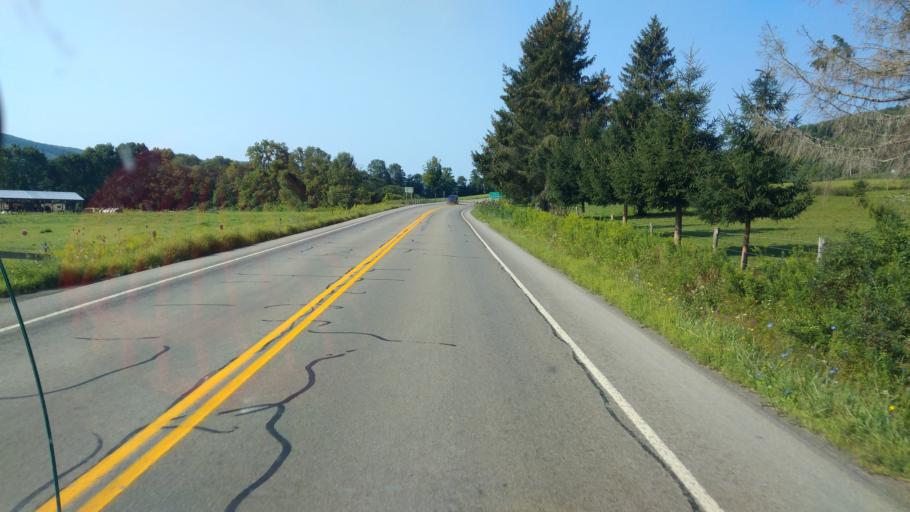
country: US
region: New York
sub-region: Allegany County
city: Friendship
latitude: 42.2974
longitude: -78.1912
